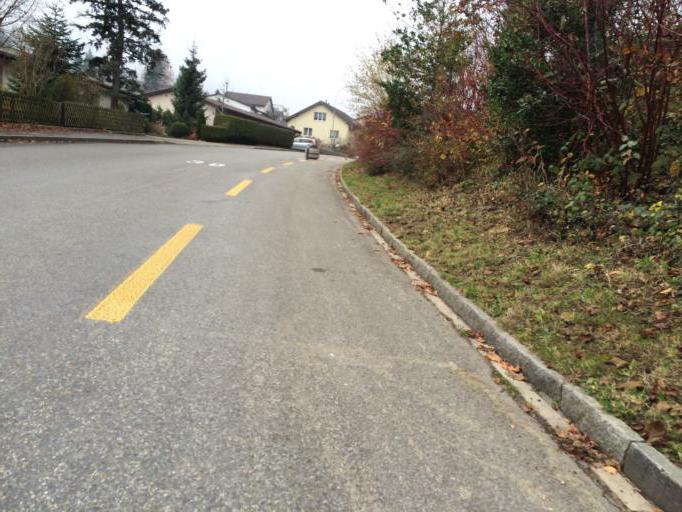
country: CH
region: Bern
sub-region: Bern-Mittelland District
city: Kehrsatz
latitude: 46.9075
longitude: 7.4645
